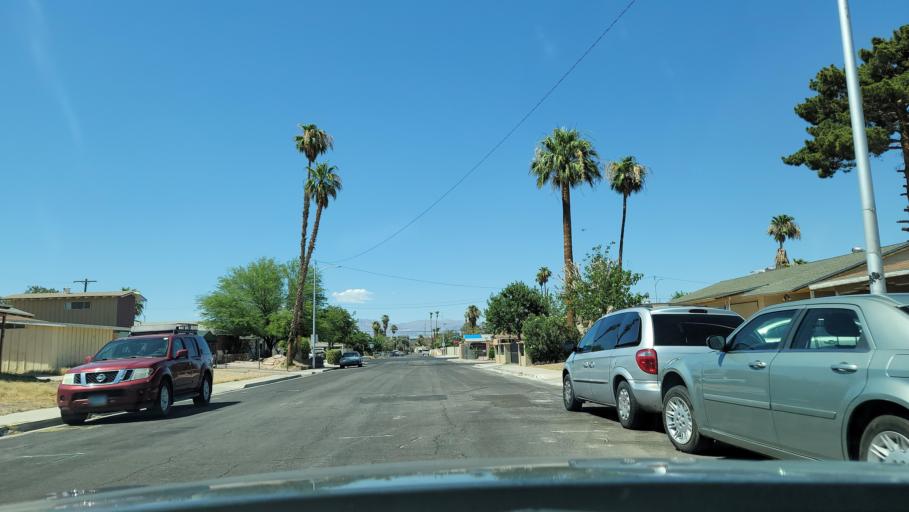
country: US
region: Nevada
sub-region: Clark County
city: Las Vegas
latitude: 36.1801
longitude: -115.1237
